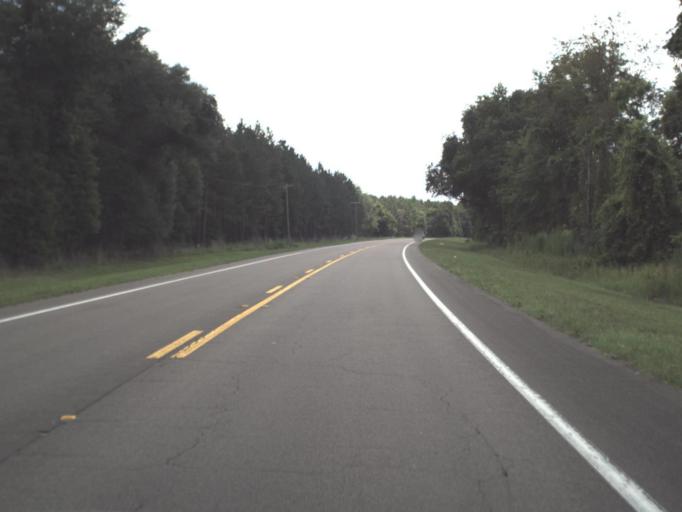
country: US
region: Florida
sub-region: Alachua County
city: Alachua
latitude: 29.8269
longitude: -82.3923
